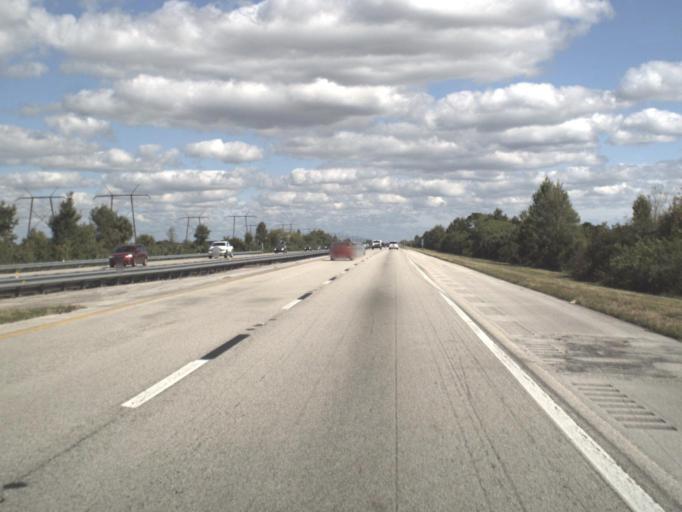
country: US
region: Florida
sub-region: Indian River County
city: Fellsmere
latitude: 27.5593
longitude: -80.7625
